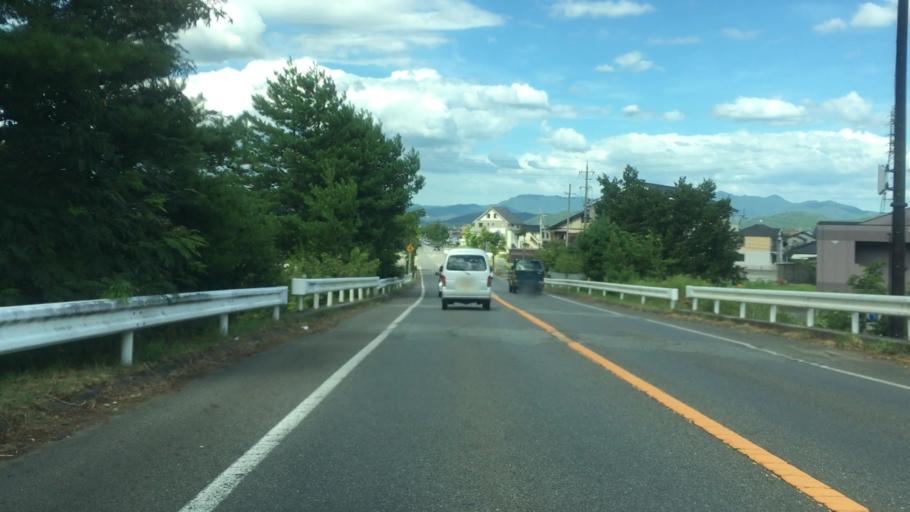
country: JP
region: Hyogo
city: Toyooka
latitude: 35.4762
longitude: 134.7773
